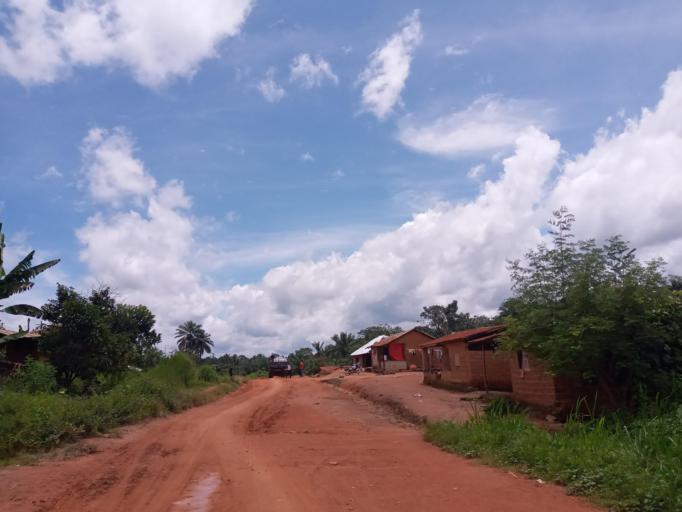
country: SL
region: Eastern Province
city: Koidu
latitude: 8.6448
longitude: -10.9163
